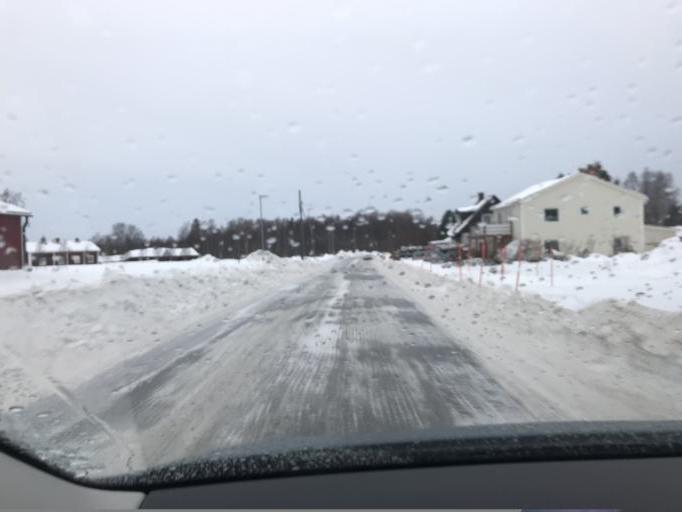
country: SE
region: Norrbotten
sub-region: Lulea Kommun
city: Sodra Sunderbyn
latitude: 65.6599
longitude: 21.9341
